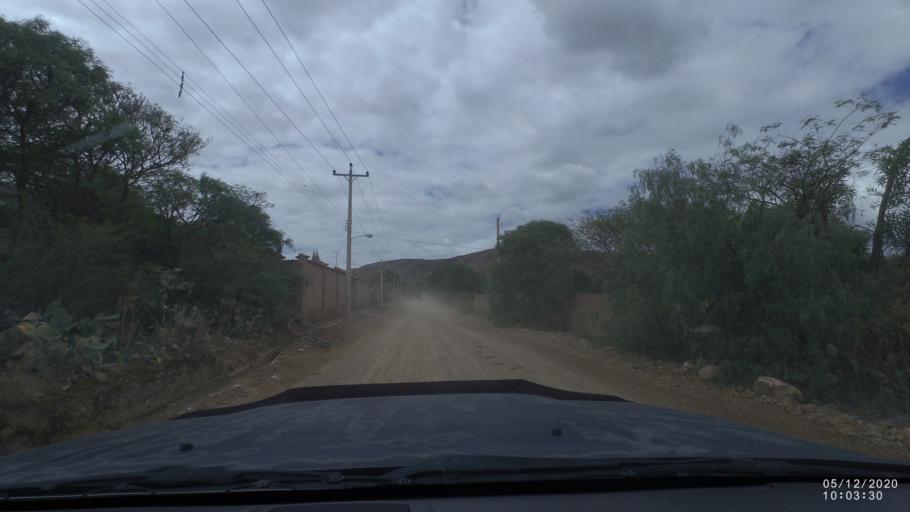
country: BO
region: Cochabamba
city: Sipe Sipe
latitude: -17.4579
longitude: -66.2868
